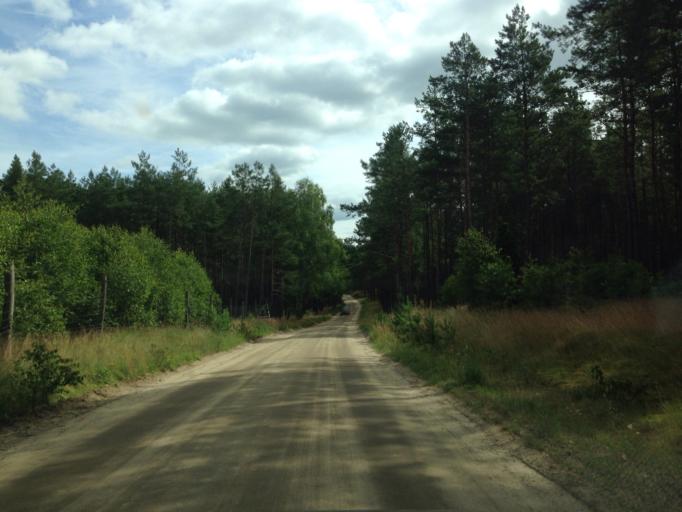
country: PL
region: Pomeranian Voivodeship
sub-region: Powiat koscierski
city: Lipusz
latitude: 54.0739
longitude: 17.6867
